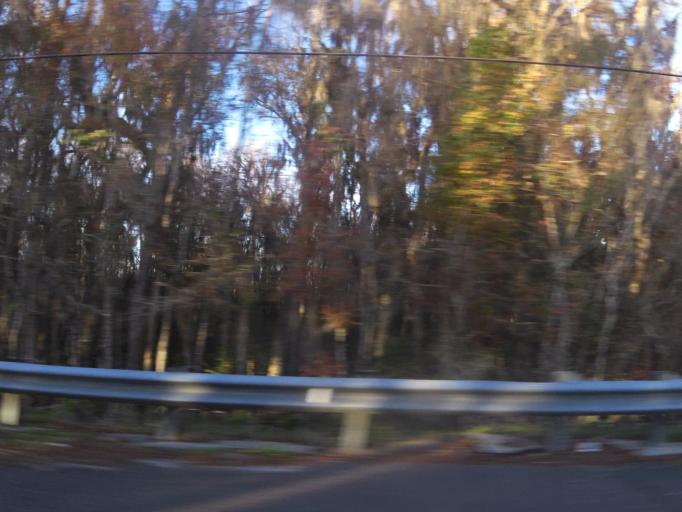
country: US
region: Florida
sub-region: Putnam County
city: East Palatka
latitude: 29.7995
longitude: -81.5401
